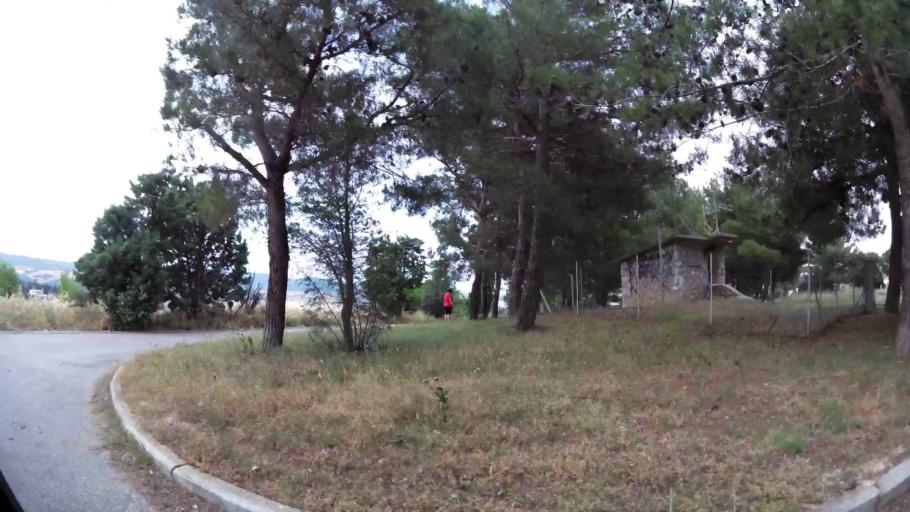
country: GR
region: Central Macedonia
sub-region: Nomos Thessalonikis
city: Oraiokastro
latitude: 40.7169
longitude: 22.9259
